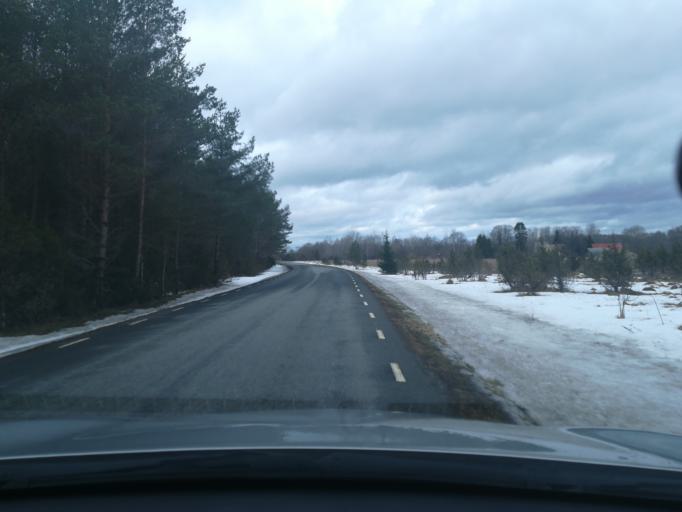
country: EE
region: Harju
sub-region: Saue linn
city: Saue
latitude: 59.3600
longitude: 24.5244
